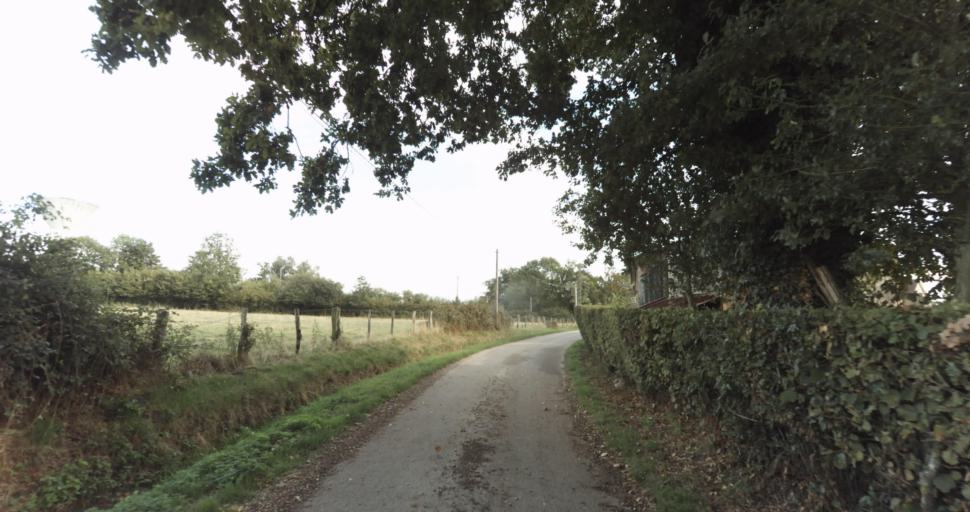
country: FR
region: Lower Normandy
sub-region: Departement de l'Orne
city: Sainte-Gauburge-Sainte-Colombe
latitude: 48.7539
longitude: 0.4005
